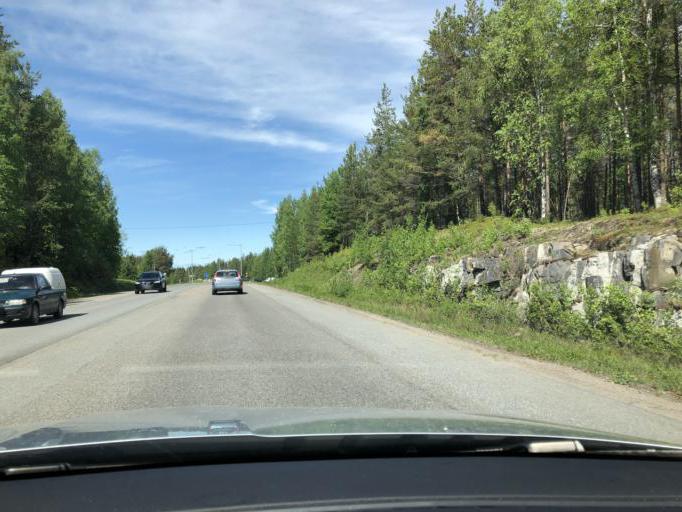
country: SE
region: Norrbotten
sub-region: Pitea Kommun
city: Pitea
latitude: 65.3287
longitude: 21.4282
